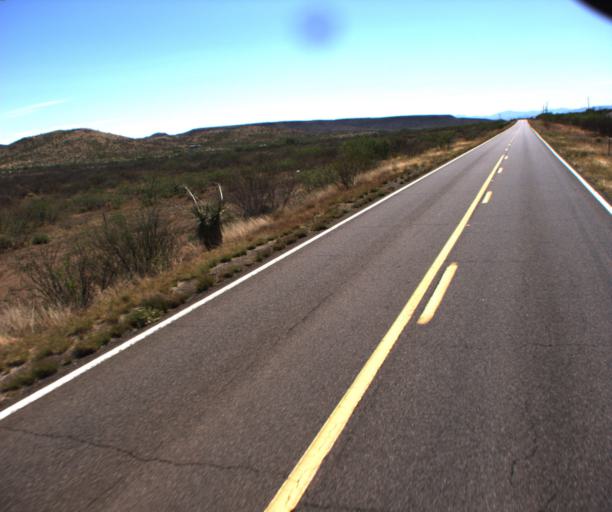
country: US
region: Arizona
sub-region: Cochise County
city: Douglas
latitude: 31.4891
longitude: -109.4211
